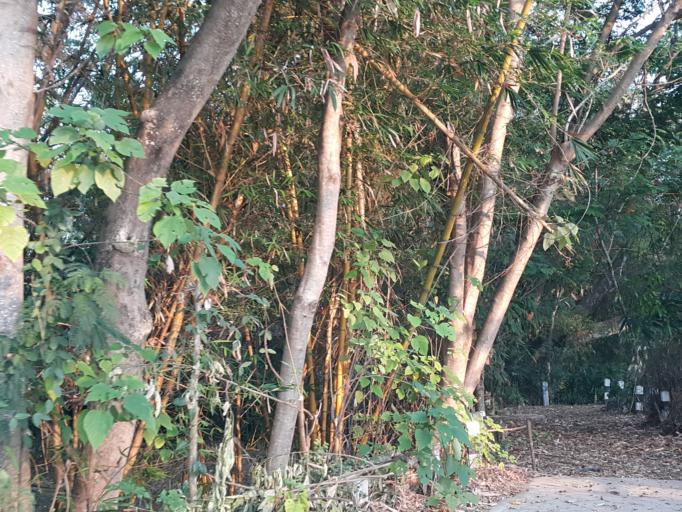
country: TH
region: Chiang Mai
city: San Sai
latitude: 18.8959
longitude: 98.9543
